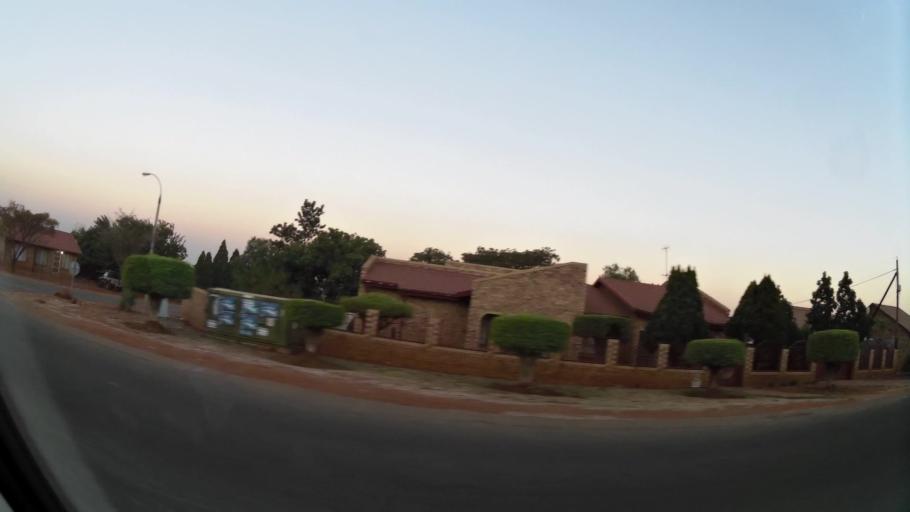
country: ZA
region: North-West
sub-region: Bojanala Platinum District Municipality
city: Rustenburg
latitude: -25.6594
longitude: 27.2053
